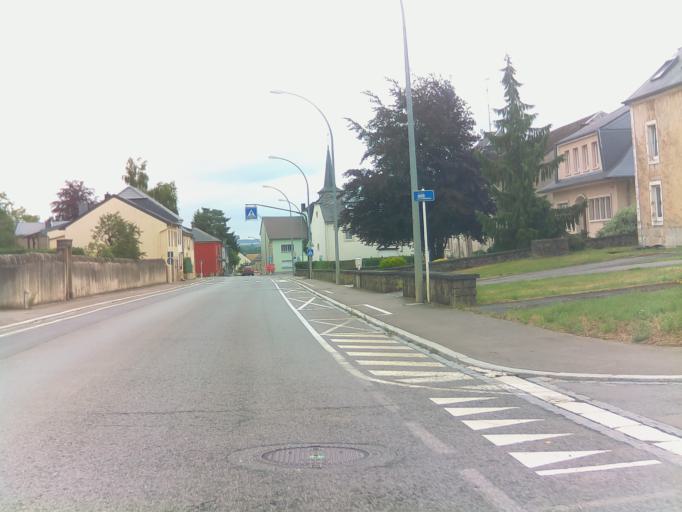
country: LU
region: Luxembourg
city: Crauthem
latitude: 49.5071
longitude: 6.1460
